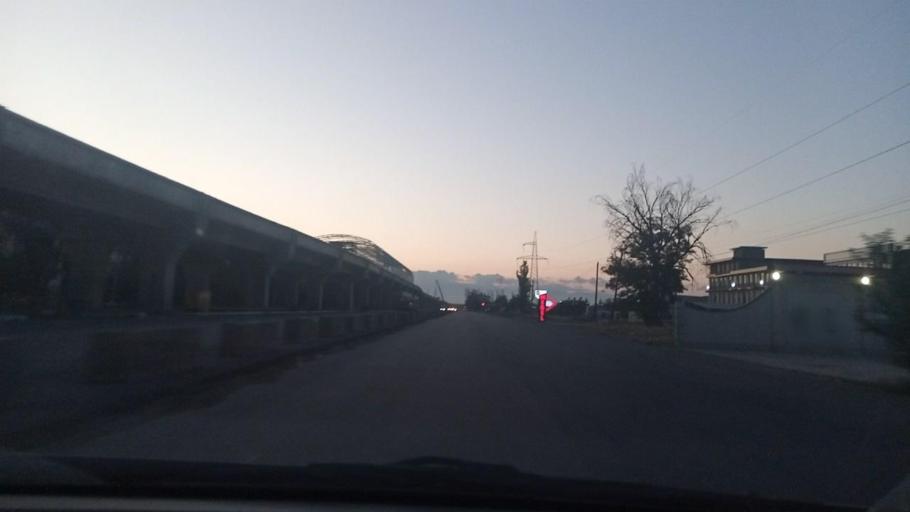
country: UZ
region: Toshkent Shahri
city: Bektemir
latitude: 41.2442
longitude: 69.2970
